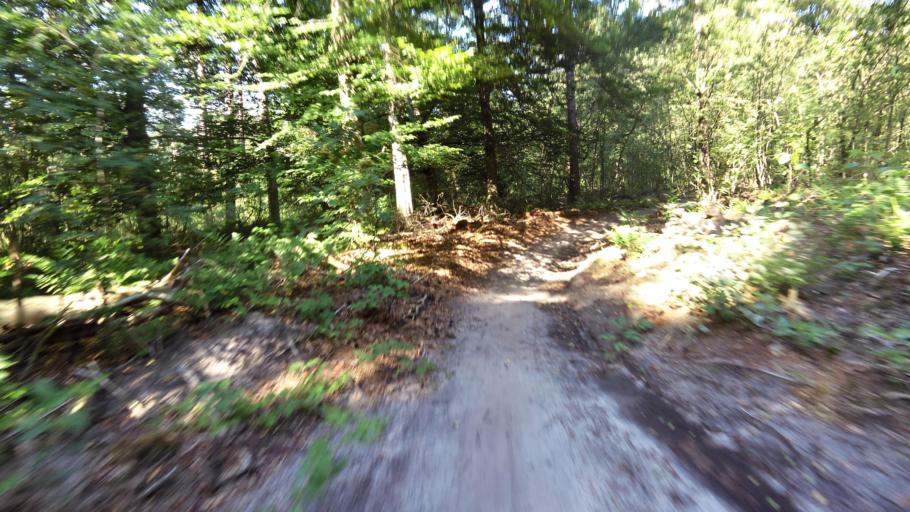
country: NL
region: Gelderland
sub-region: Gemeente Arnhem
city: Hoogkamp
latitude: 52.0118
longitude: 5.8796
